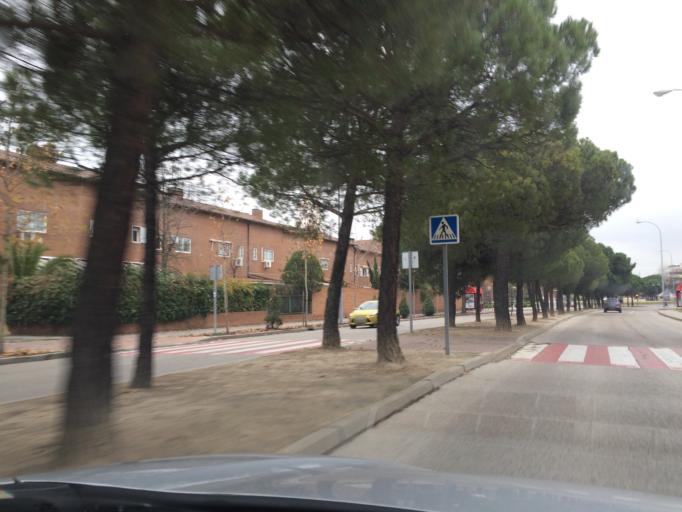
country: ES
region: Madrid
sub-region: Provincia de Madrid
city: Tres Cantos
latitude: 40.5973
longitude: -3.7071
